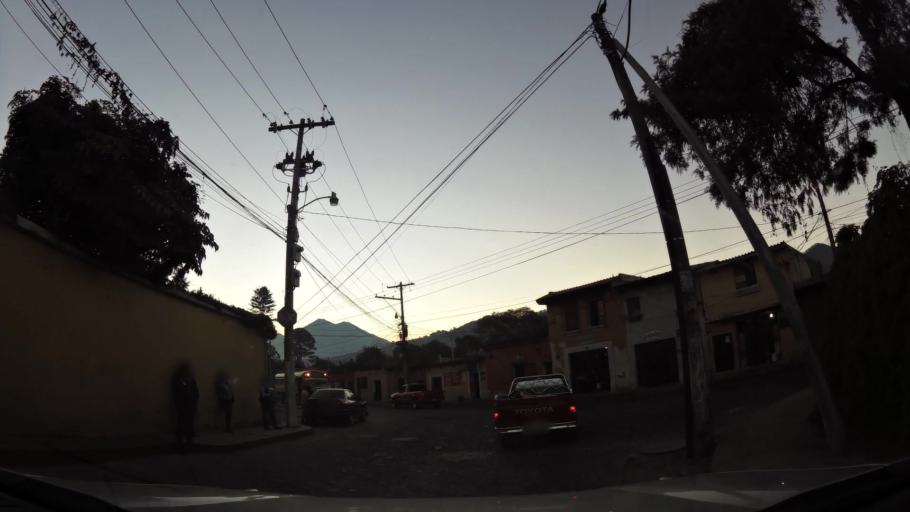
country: GT
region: Sacatepequez
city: Antigua Guatemala
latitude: 14.5521
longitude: -90.7397
